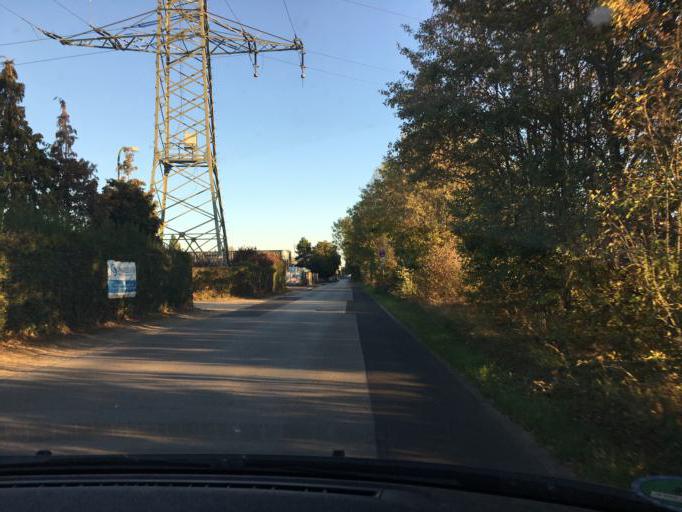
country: DE
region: North Rhine-Westphalia
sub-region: Regierungsbezirk Koln
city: Dueren
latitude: 50.8032
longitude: 6.4532
